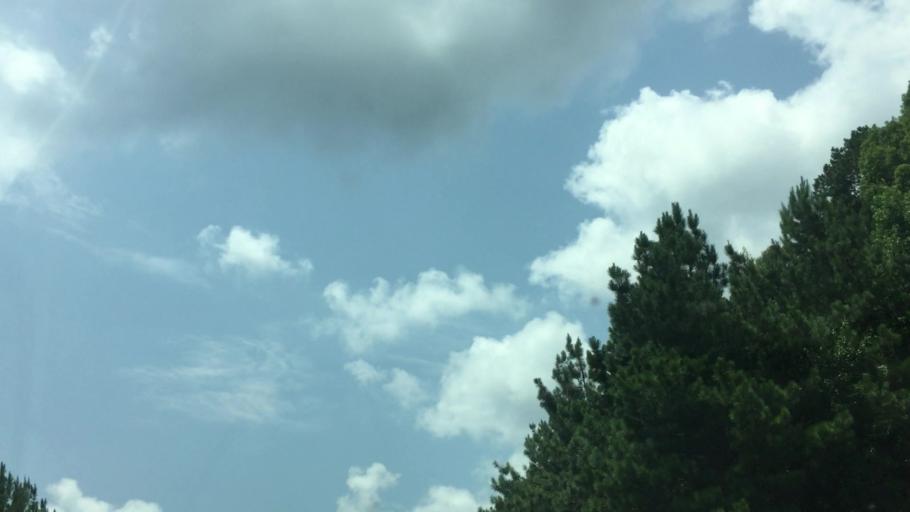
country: US
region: Georgia
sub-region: Fulton County
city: Chattahoochee Hills
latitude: 33.5679
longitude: -84.7354
